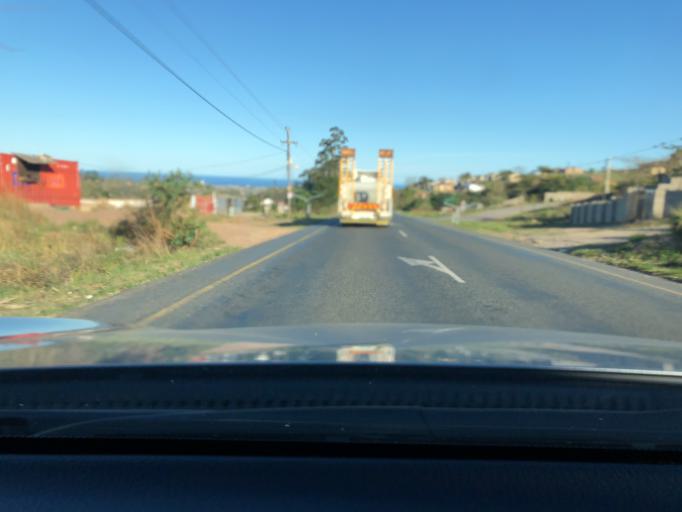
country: ZA
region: KwaZulu-Natal
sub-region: eThekwini Metropolitan Municipality
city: Umkomaas
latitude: -30.0134
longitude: 30.8065
